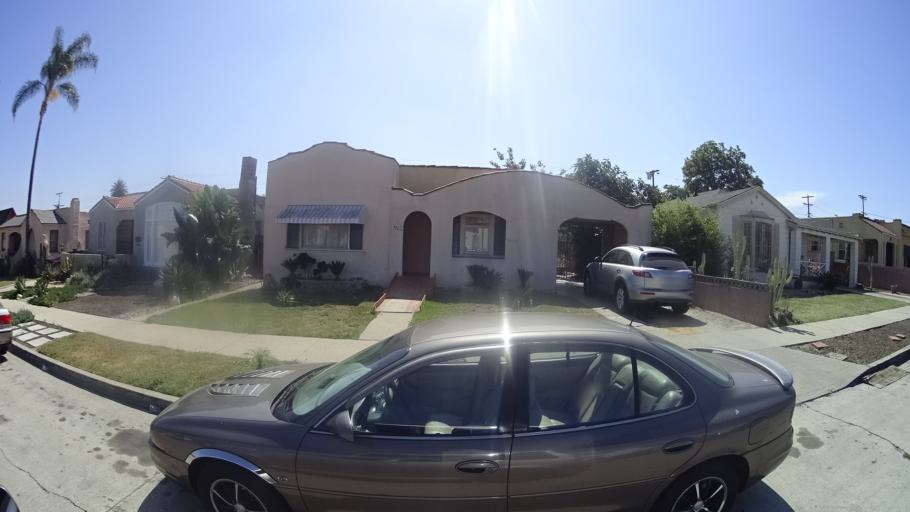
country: US
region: California
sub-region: Los Angeles County
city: View Park-Windsor Hills
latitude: 33.9756
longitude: -118.3207
